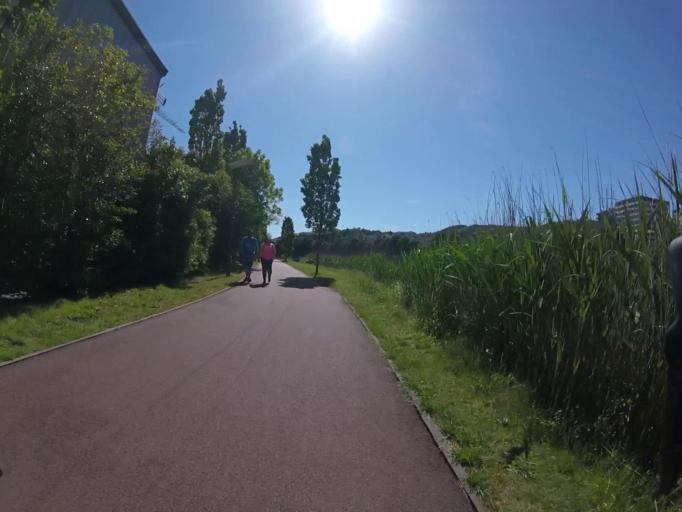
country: ES
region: Basque Country
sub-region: Provincia de Guipuzcoa
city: Irun
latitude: 43.3428
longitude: -1.7721
